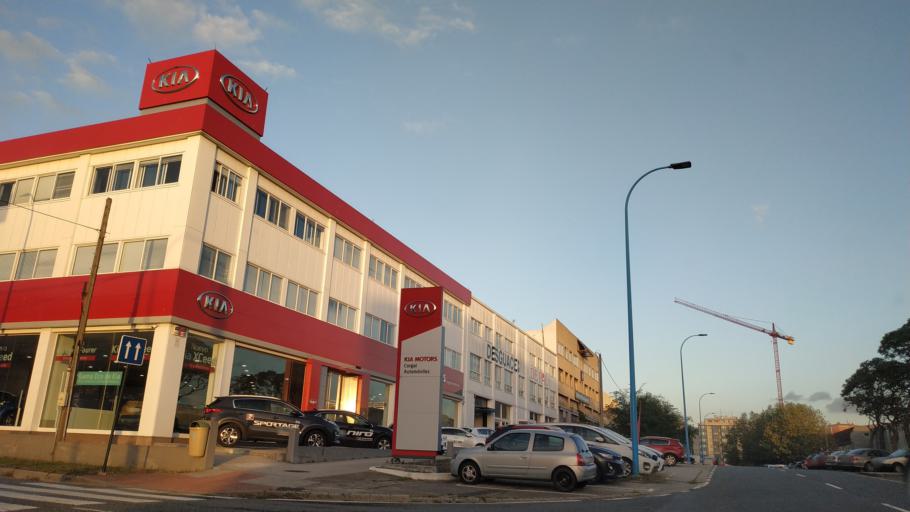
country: ES
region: Galicia
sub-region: Provincia da Coruna
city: A Coruna
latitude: 43.3542
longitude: -8.4201
